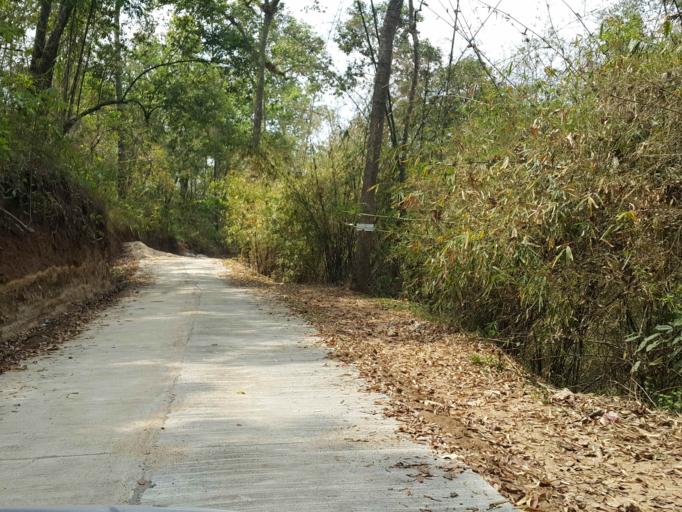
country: TH
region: Chiang Mai
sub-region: Amphoe Chiang Dao
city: Chiang Dao
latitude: 19.2968
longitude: 98.7518
